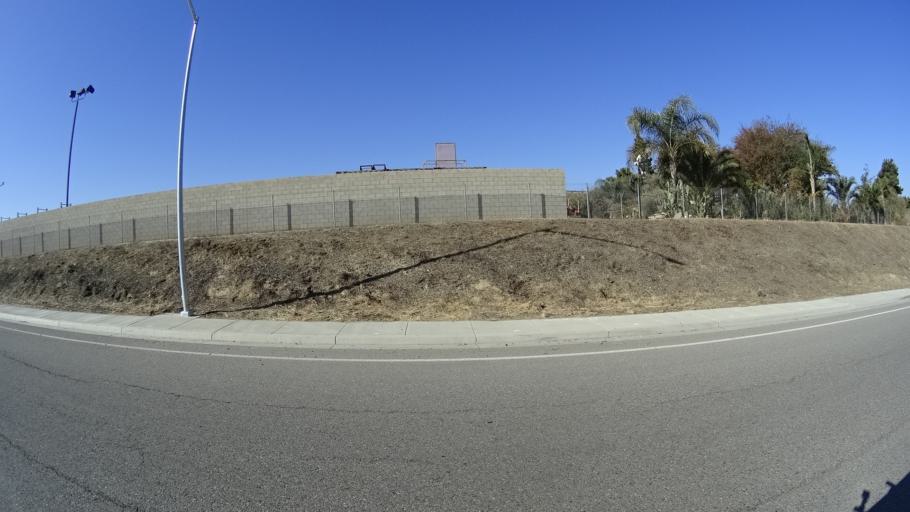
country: US
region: California
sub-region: Kern County
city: Rosedale
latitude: 35.3968
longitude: -119.1460
